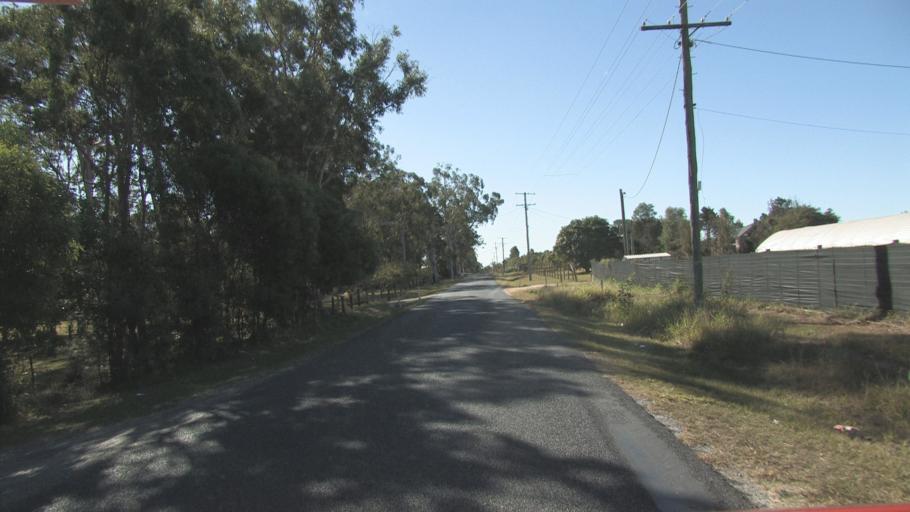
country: AU
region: Queensland
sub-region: Logan
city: Logan Reserve
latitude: -27.7248
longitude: 153.0733
